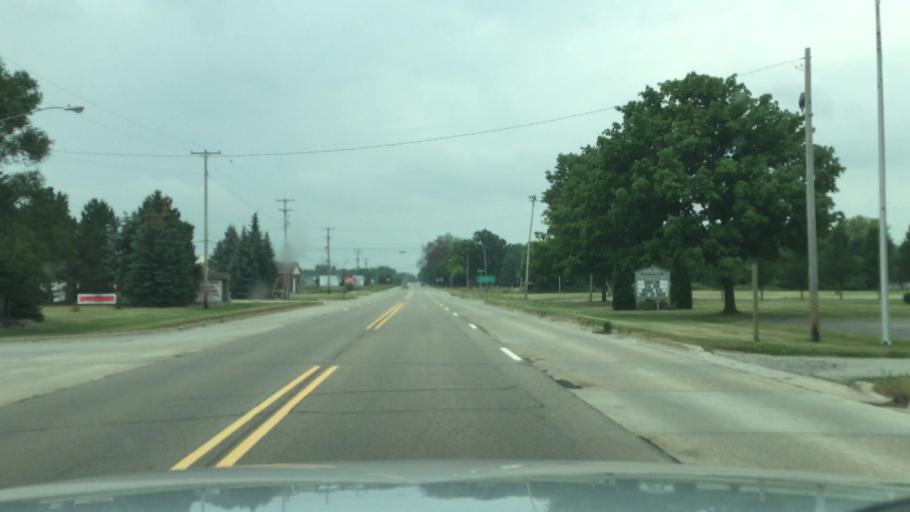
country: US
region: Michigan
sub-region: Shiawassee County
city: Owosso
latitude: 43.0288
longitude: -84.1769
